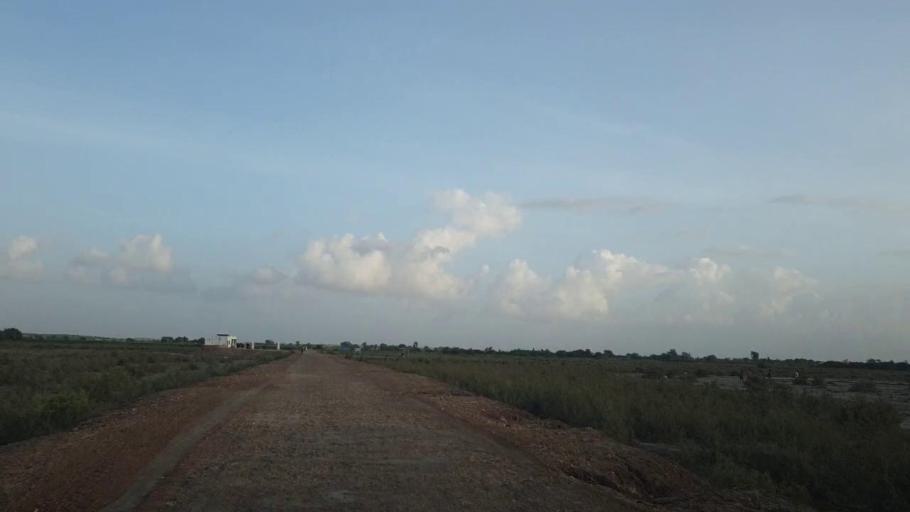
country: PK
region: Sindh
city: Kadhan
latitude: 24.5511
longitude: 69.1239
